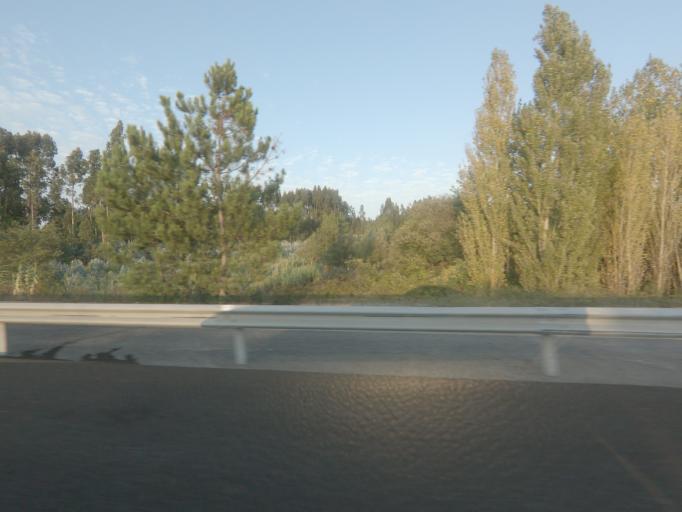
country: PT
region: Leiria
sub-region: Leiria
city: Caranguejeira
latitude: 39.7694
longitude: -8.7443
